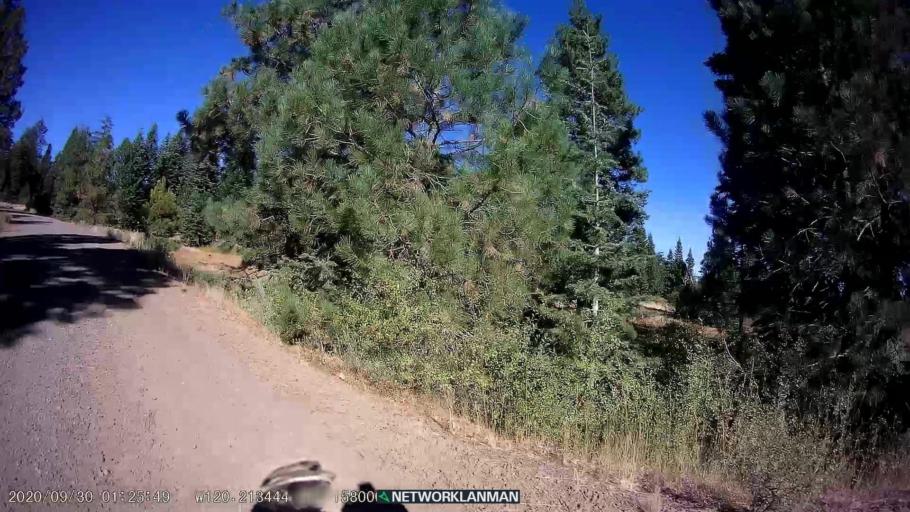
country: US
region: Oregon
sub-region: Lake County
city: Lakeview
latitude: 42.1578
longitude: -120.2184
